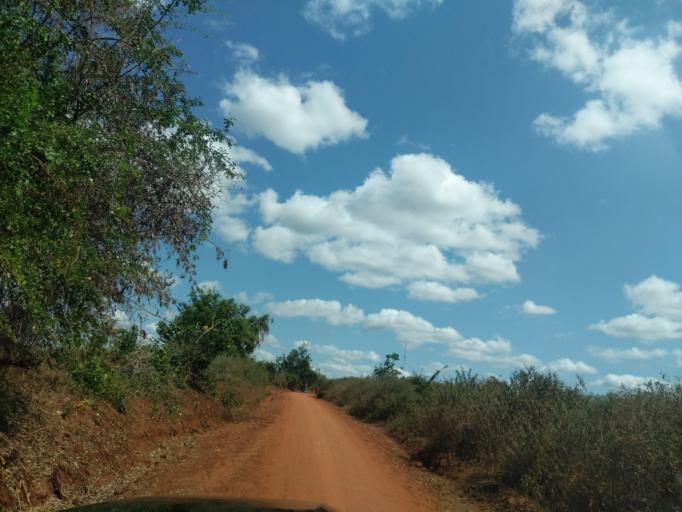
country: TZ
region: Tanga
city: Chanika
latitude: -5.5175
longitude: 38.3588
